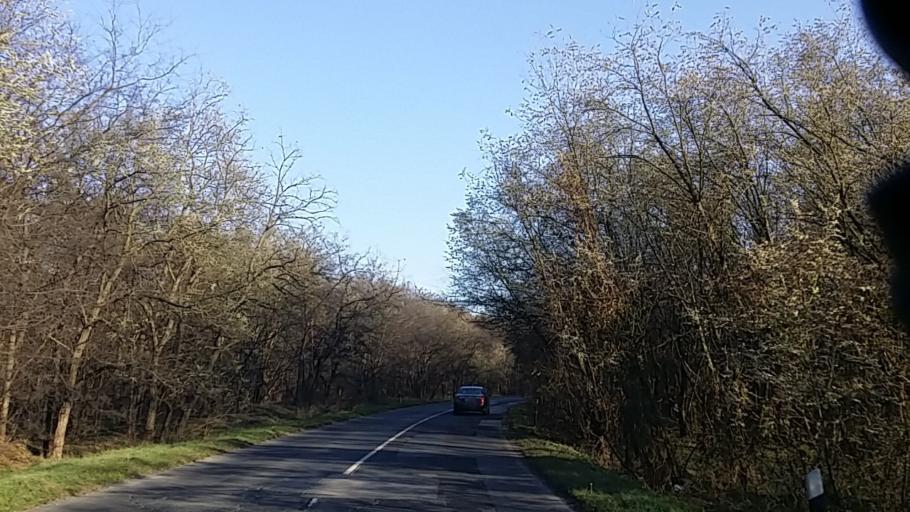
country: HU
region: Budapest
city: Budapest XVIII. keruelet
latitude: 47.4588
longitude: 19.2083
